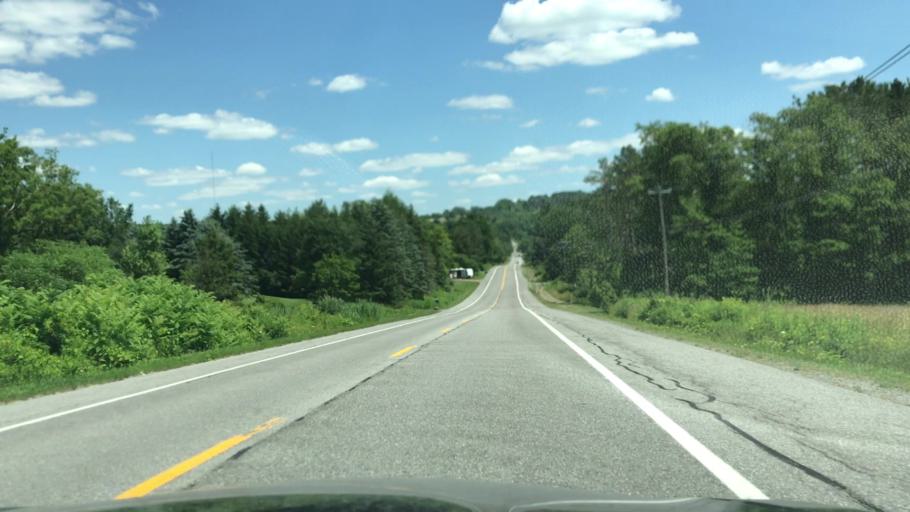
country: US
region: New York
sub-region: Erie County
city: East Aurora
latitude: 42.7693
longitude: -78.4983
